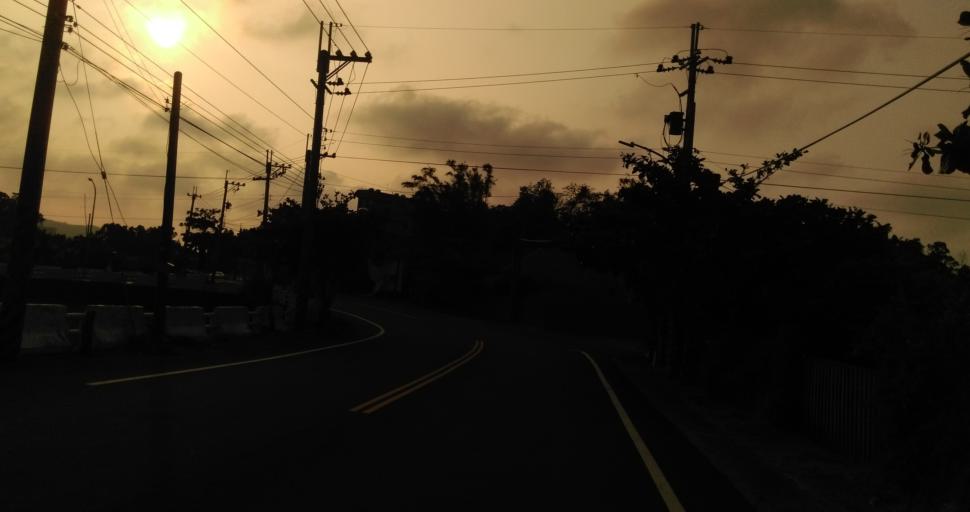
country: TW
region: Taiwan
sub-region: Hsinchu
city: Hsinchu
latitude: 24.7456
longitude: 120.9218
